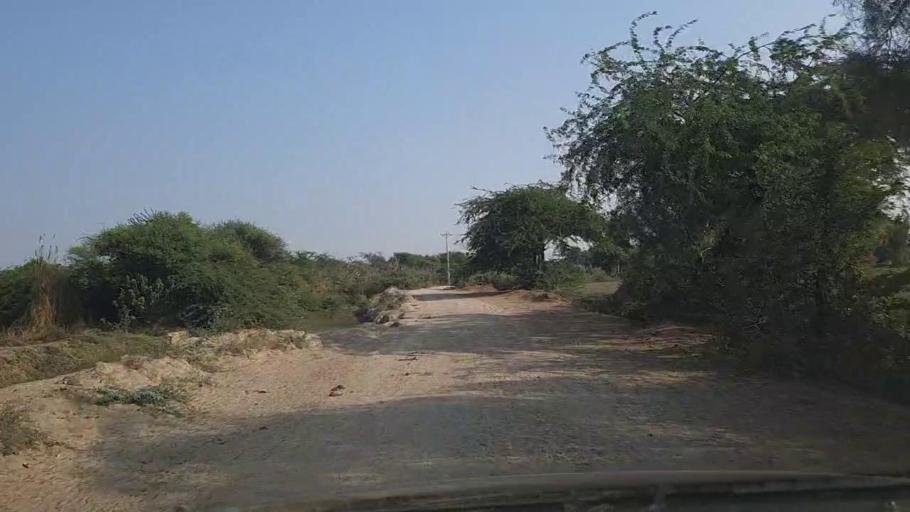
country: PK
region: Sindh
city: Mirpur Sakro
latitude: 24.6339
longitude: 67.7548
